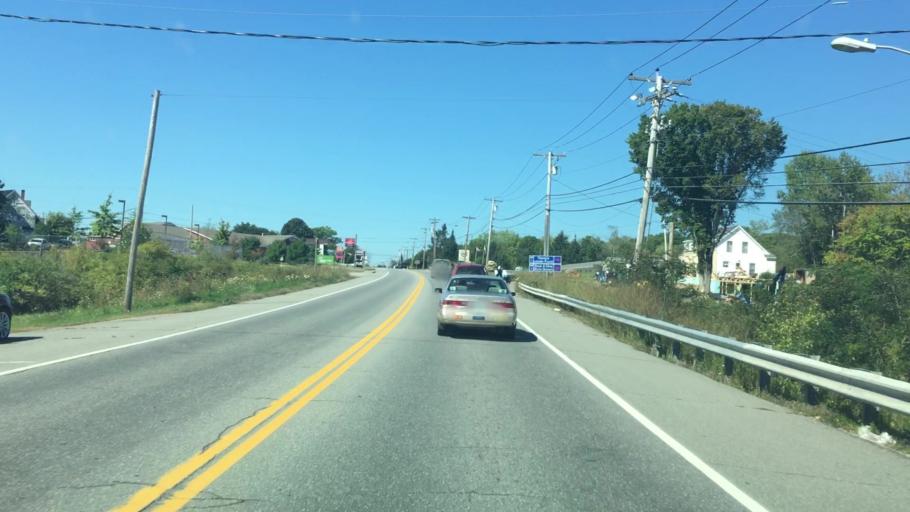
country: US
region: Maine
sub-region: Waldo County
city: Belfast
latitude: 44.4329
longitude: -68.9946
